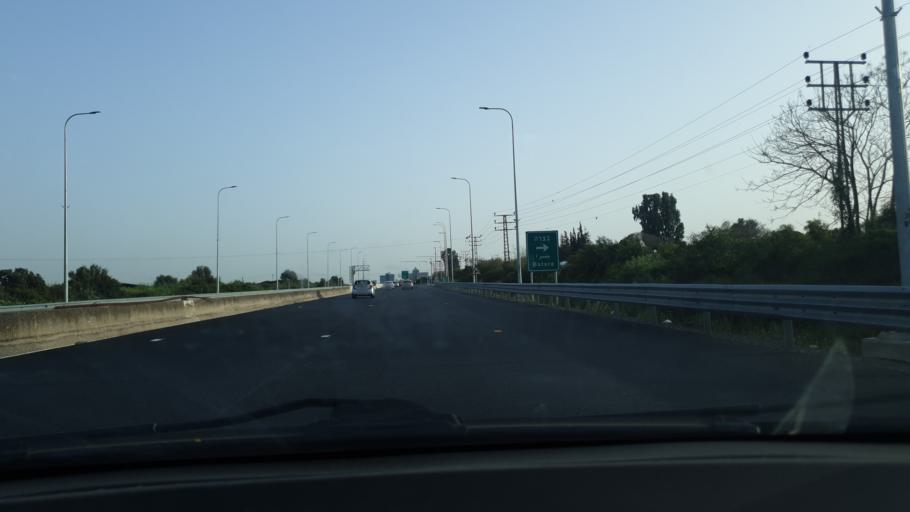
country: IL
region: Central District
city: Ra'anana
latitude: 32.2129
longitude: 34.8835
